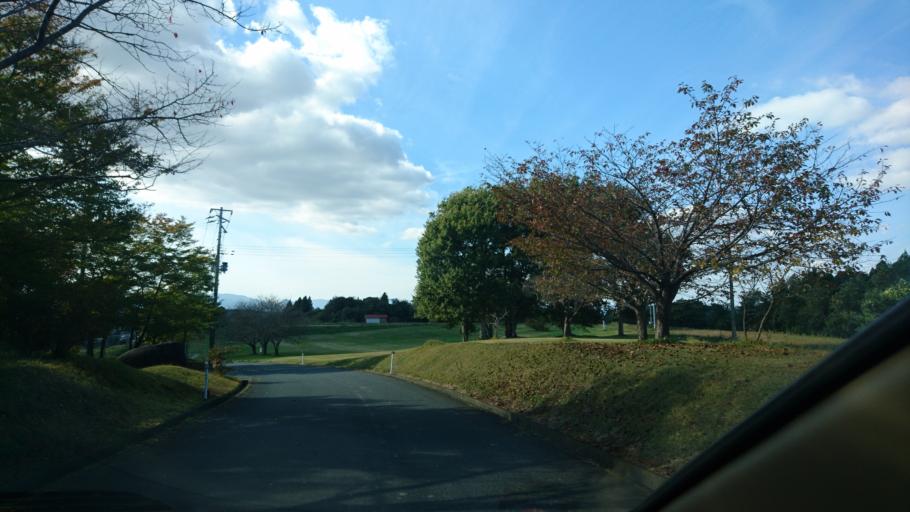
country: JP
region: Iwate
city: Kitakami
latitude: 39.2421
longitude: 141.1307
